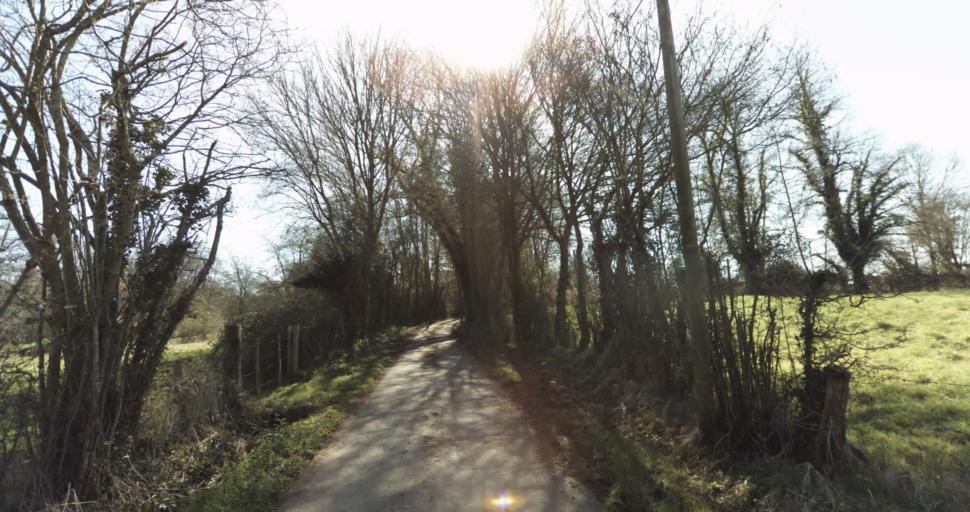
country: FR
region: Lower Normandy
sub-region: Departement du Calvados
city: Livarot
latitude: 48.9907
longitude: 0.0767
